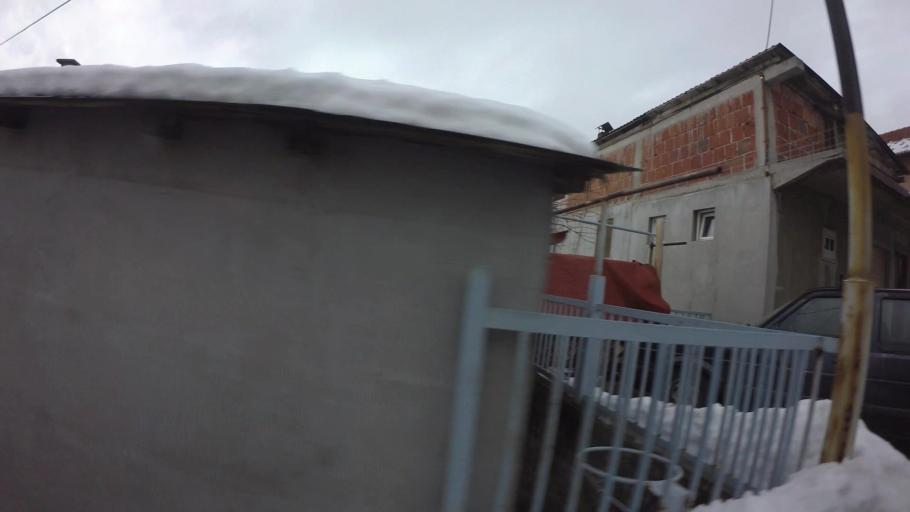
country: BA
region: Federation of Bosnia and Herzegovina
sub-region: Kanton Sarajevo
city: Sarajevo
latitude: 43.8539
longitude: 18.3549
